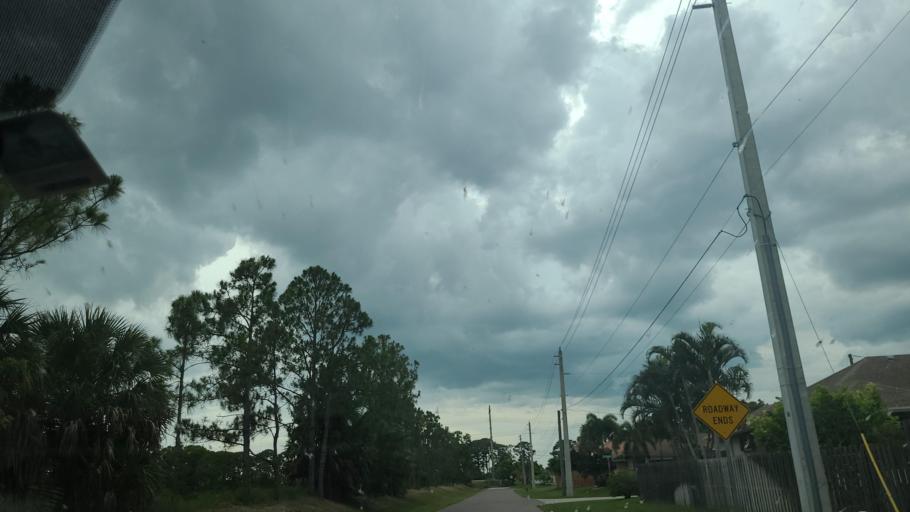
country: US
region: Florida
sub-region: Saint Lucie County
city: Port Saint Lucie
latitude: 27.2499
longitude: -80.4131
